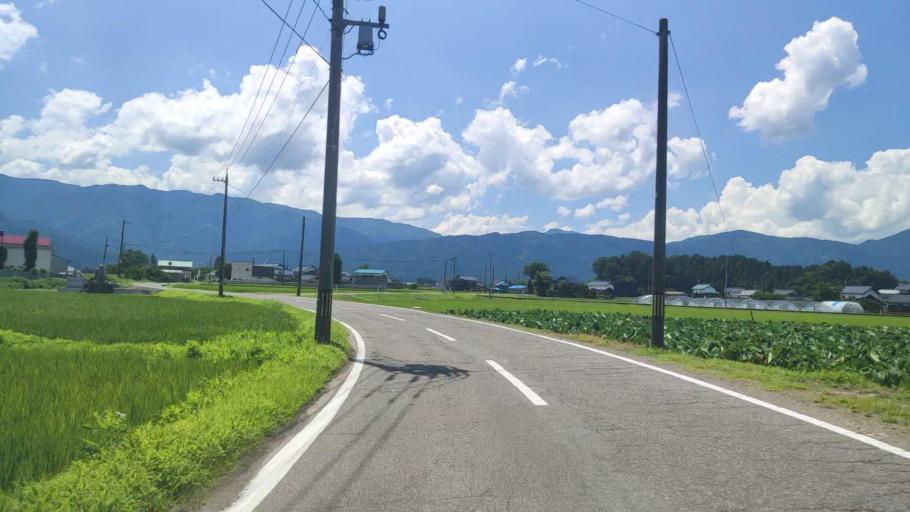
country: JP
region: Fukui
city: Ono
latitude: 35.9727
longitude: 136.5239
